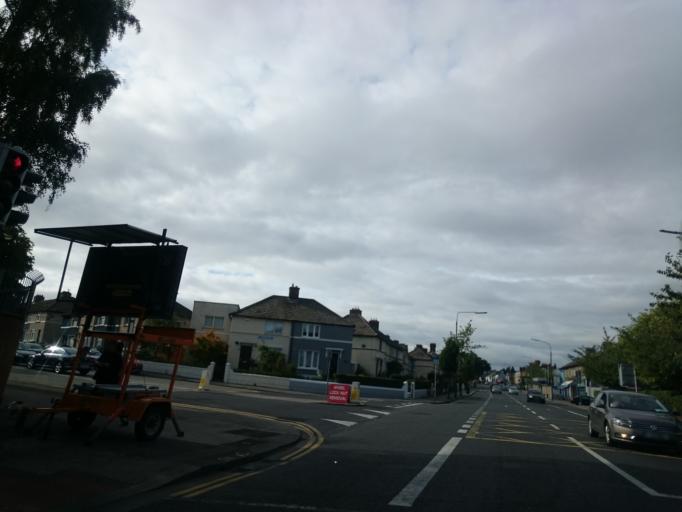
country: IE
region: Leinster
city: Rathgar
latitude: 53.3282
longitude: -6.2765
